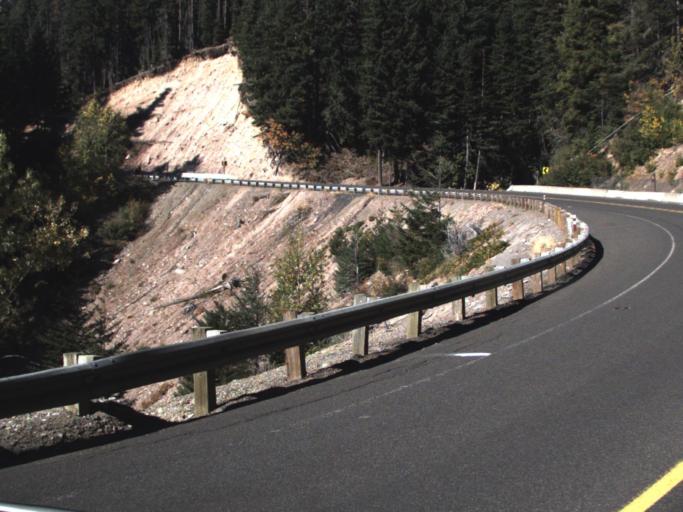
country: US
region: Washington
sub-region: Yakima County
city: Tieton
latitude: 46.6592
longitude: -121.3406
